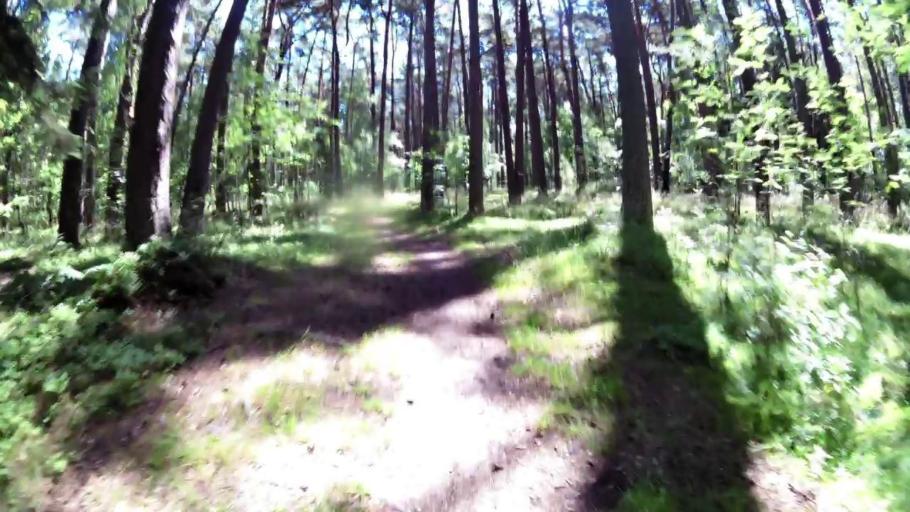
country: PL
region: West Pomeranian Voivodeship
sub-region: Powiat kamienski
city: Dziwnow
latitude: 54.0433
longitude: 14.8491
